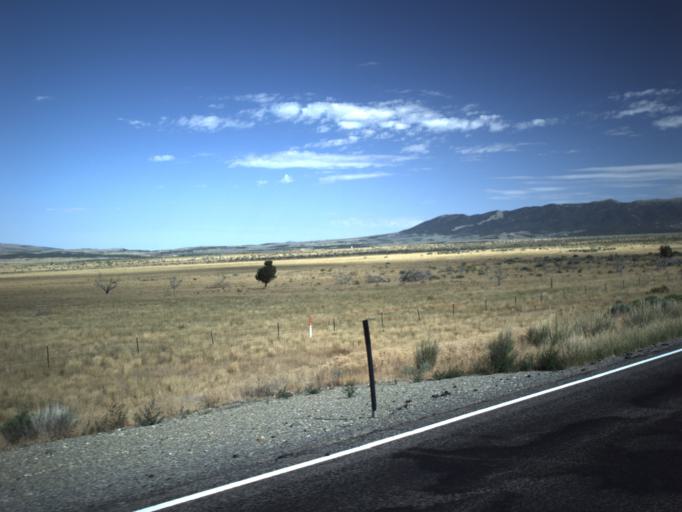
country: US
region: Utah
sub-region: Juab County
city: Mona
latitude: 39.8818
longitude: -112.1380
